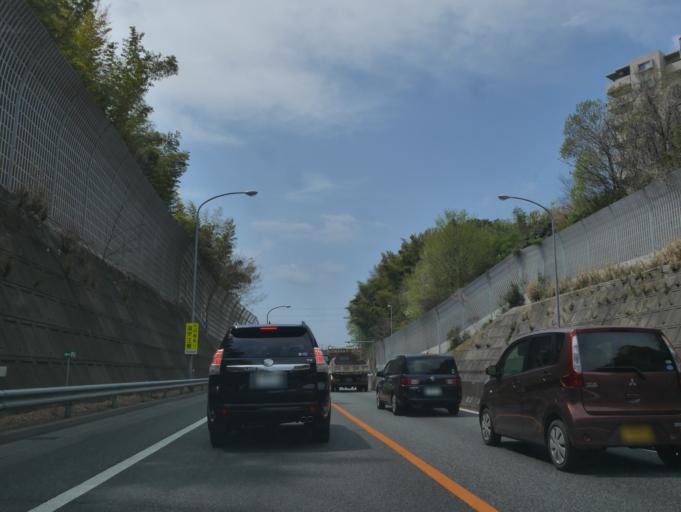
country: JP
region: Kanagawa
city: Fujisawa
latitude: 35.4148
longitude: 139.5356
